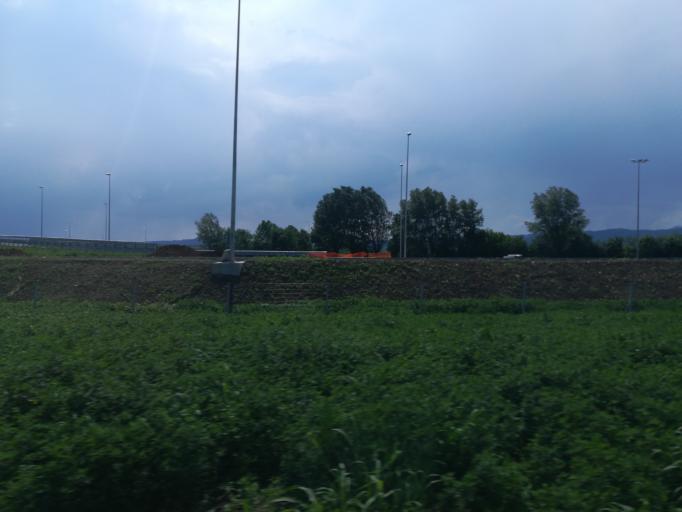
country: IT
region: Veneto
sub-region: Provincia di Vicenza
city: Novoledo
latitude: 45.6632
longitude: 11.5179
